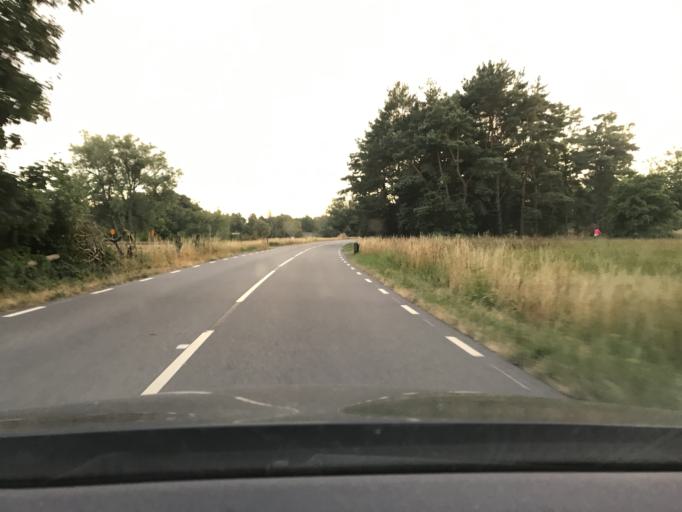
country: SE
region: Skane
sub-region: Simrishamns Kommun
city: Simrishamn
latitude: 55.4159
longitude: 14.2069
